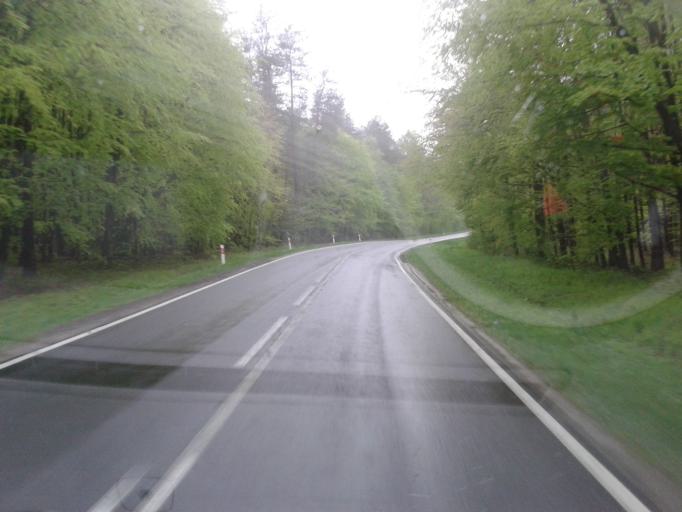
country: PL
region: Subcarpathian Voivodeship
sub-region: Powiat lubaczowski
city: Narol
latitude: 50.3415
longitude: 23.3107
